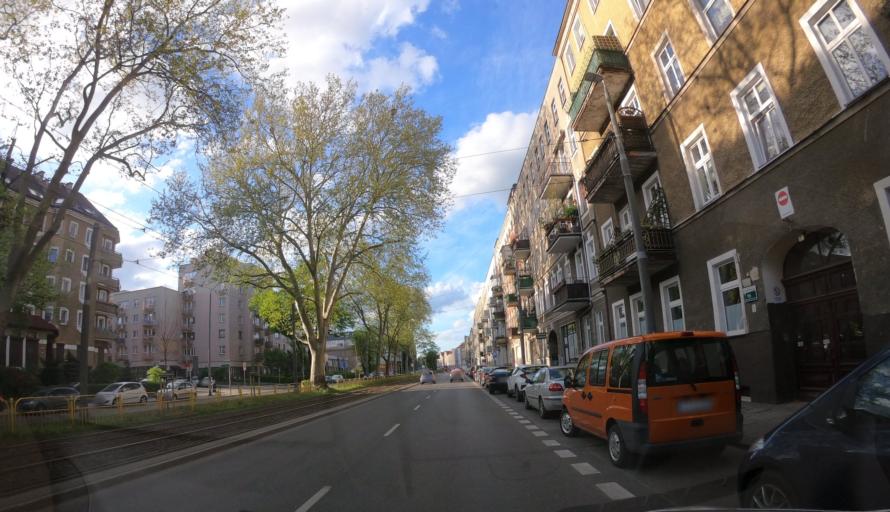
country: PL
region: West Pomeranian Voivodeship
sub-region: Szczecin
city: Szczecin
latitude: 53.4302
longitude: 14.5321
